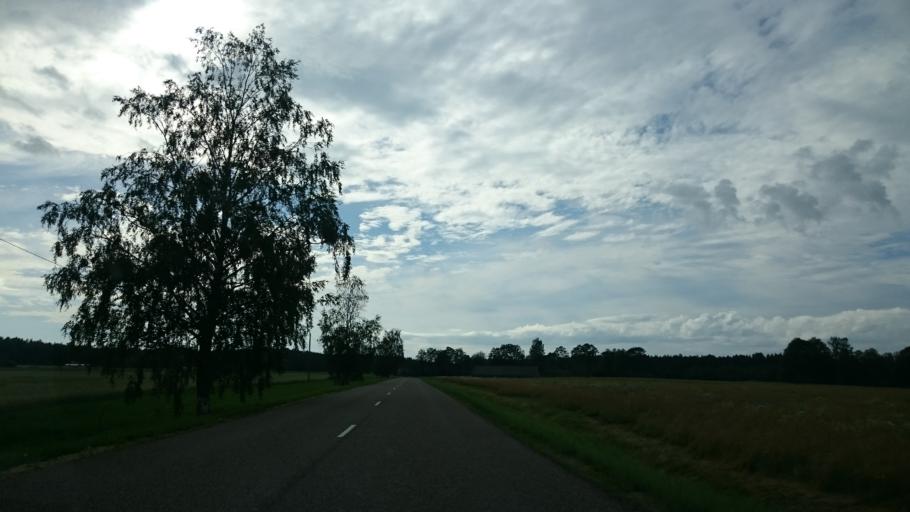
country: LV
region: Saulkrastu
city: Saulkrasti
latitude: 57.2495
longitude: 24.5132
